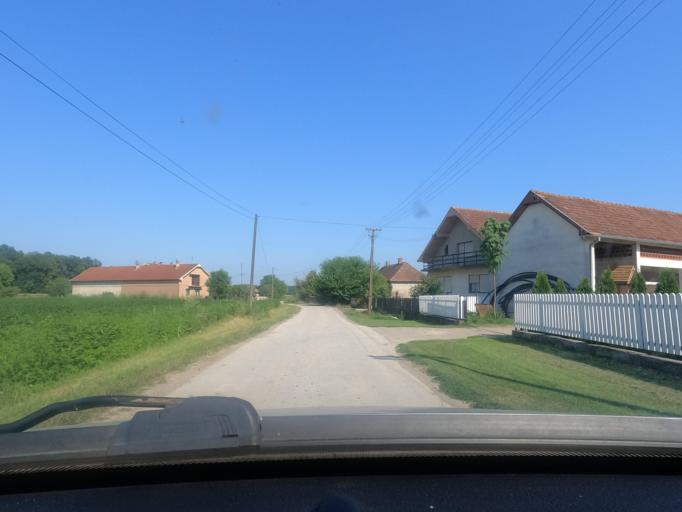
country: RS
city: Bogosavac
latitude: 44.7485
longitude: 19.5834
